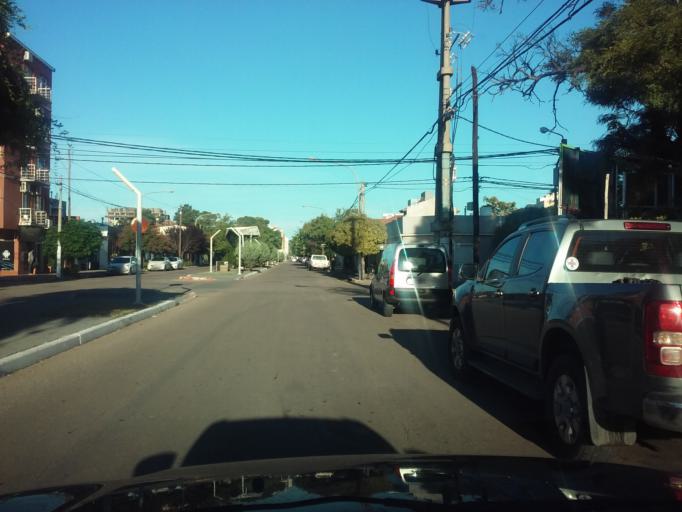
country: AR
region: La Pampa
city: Santa Rosa
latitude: -36.6210
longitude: -64.2994
